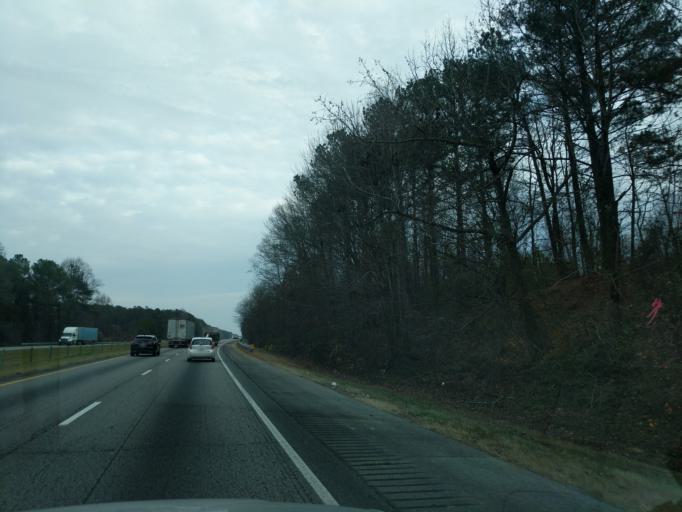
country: US
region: Georgia
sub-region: Jackson County
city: Braselton
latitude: 34.1244
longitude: -83.7435
